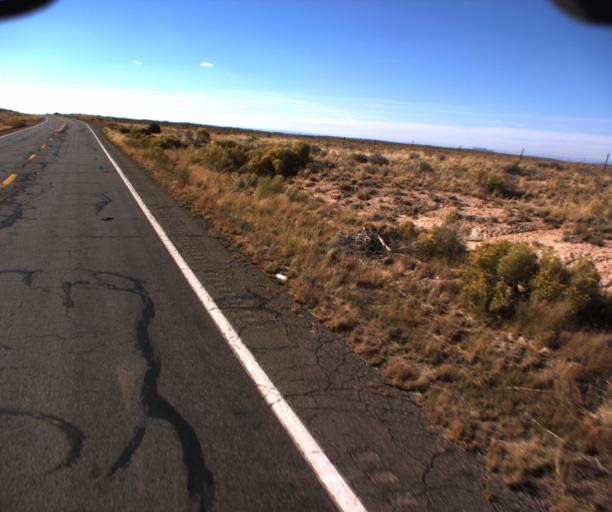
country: US
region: Arizona
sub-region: Coconino County
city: Kaibito
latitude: 36.6177
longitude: -110.9657
